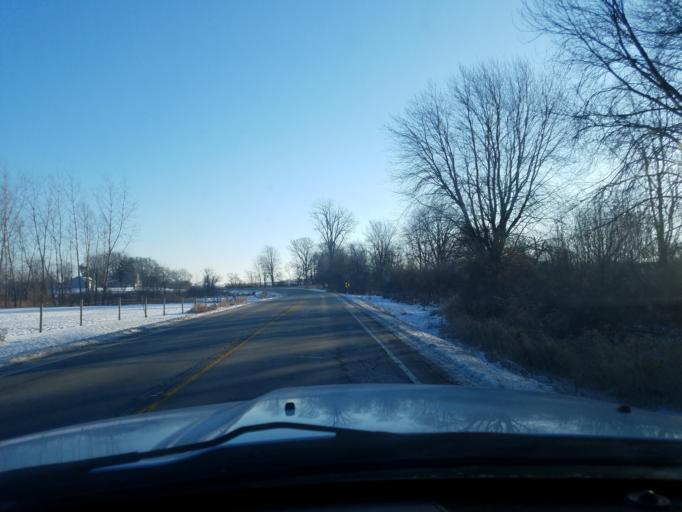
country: US
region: Indiana
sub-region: Noble County
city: Ligonier
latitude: 41.4525
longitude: -85.5512
